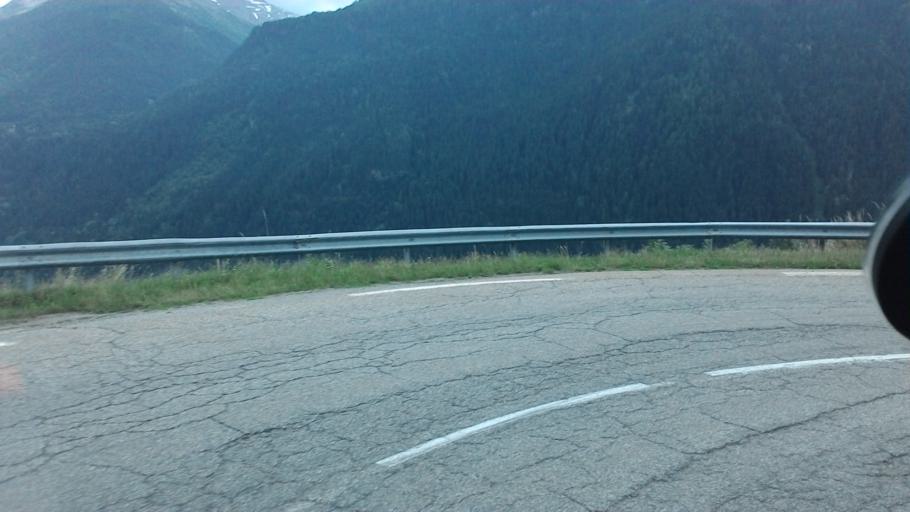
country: FR
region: Rhone-Alpes
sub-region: Departement de la Savoie
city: Seez
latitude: 45.6204
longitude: 6.8255
